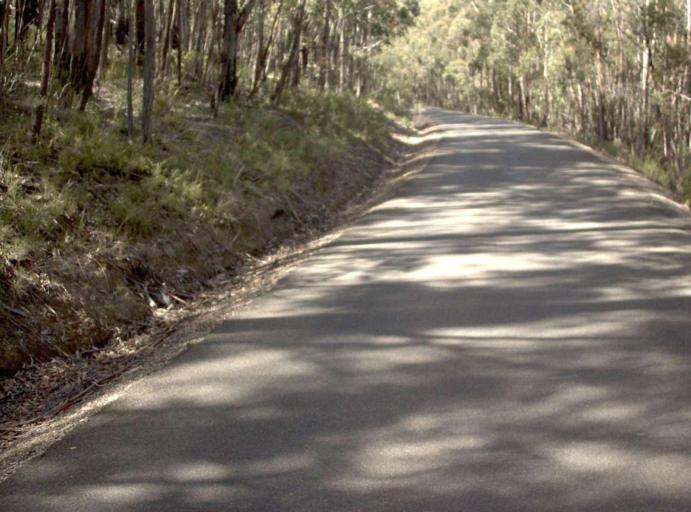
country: AU
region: Victoria
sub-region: East Gippsland
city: Lakes Entrance
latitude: -37.4405
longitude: 148.1317
